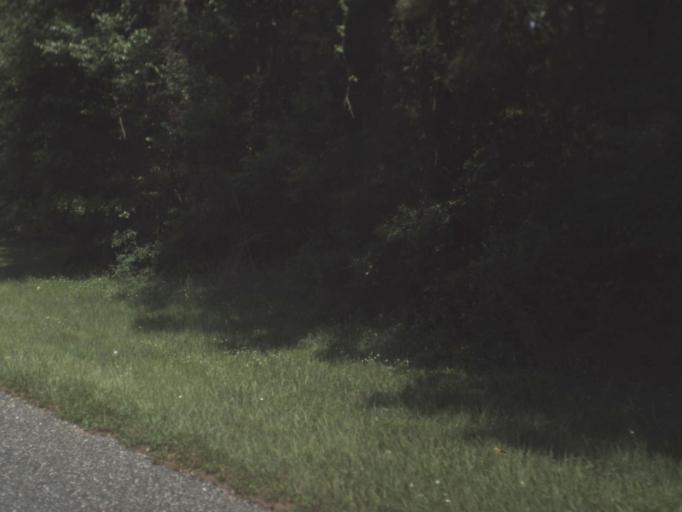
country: US
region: Florida
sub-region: Clay County
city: Middleburg
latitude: 29.9819
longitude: -81.9481
